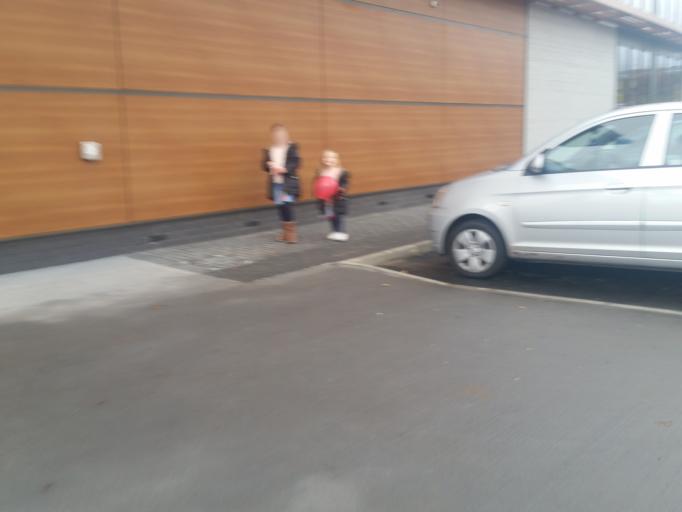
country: GB
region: England
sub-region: Derbyshire
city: Borrowash
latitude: 52.9016
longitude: -1.4252
